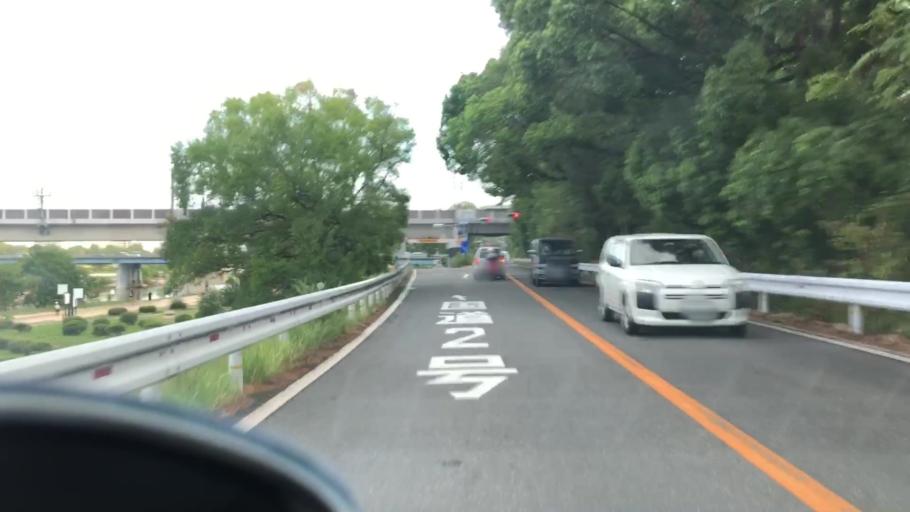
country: JP
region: Hyogo
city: Itami
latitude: 34.7671
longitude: 135.3725
